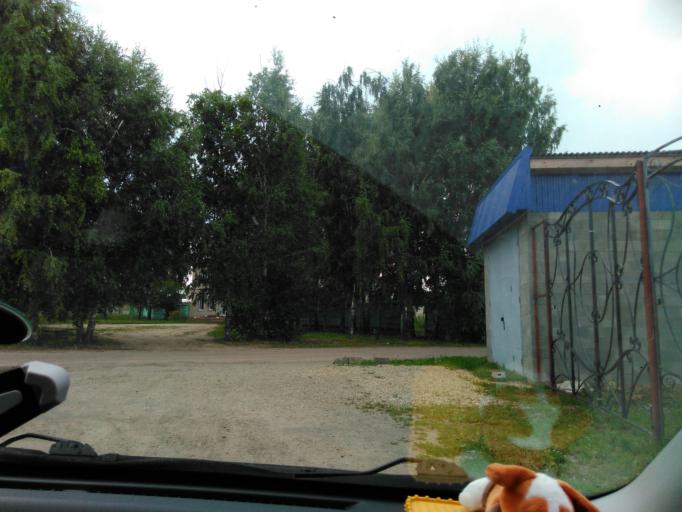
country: RU
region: Penza
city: Poim
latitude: 53.0309
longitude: 43.1748
